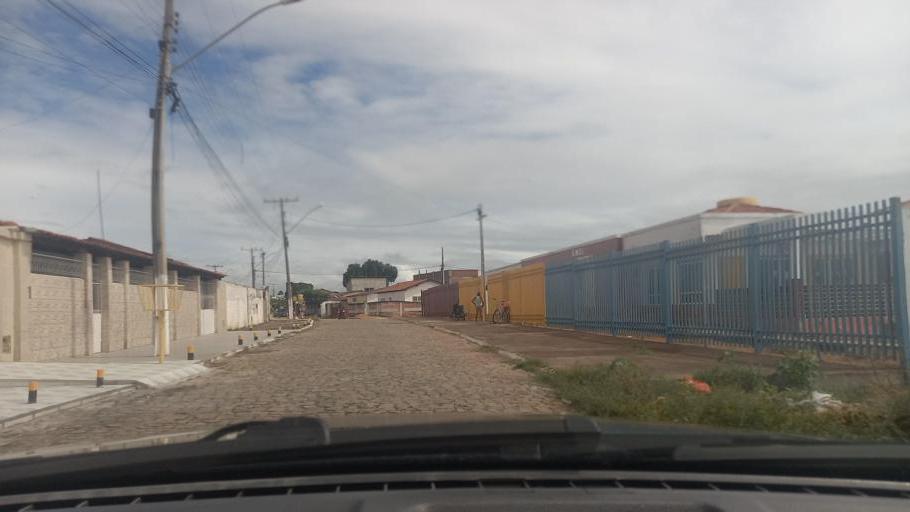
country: BR
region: Bahia
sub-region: Paulo Afonso
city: Paulo Afonso
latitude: -9.3395
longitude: -38.2565
